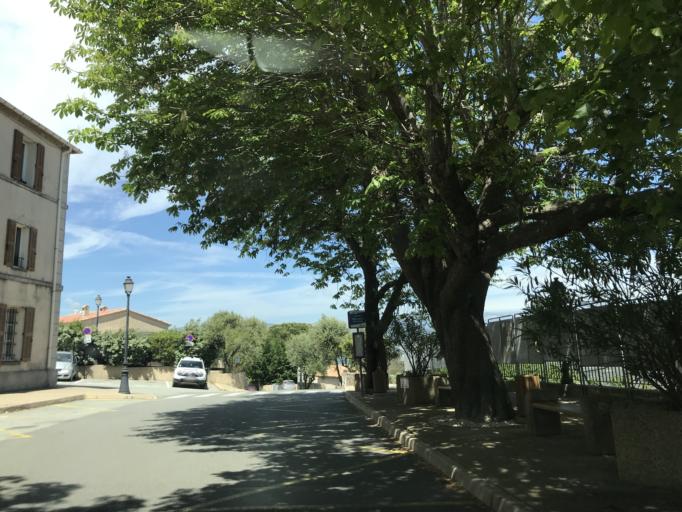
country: FR
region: Provence-Alpes-Cote d'Azur
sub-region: Departement du Var
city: Tanneron
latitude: 43.5906
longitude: 6.8755
